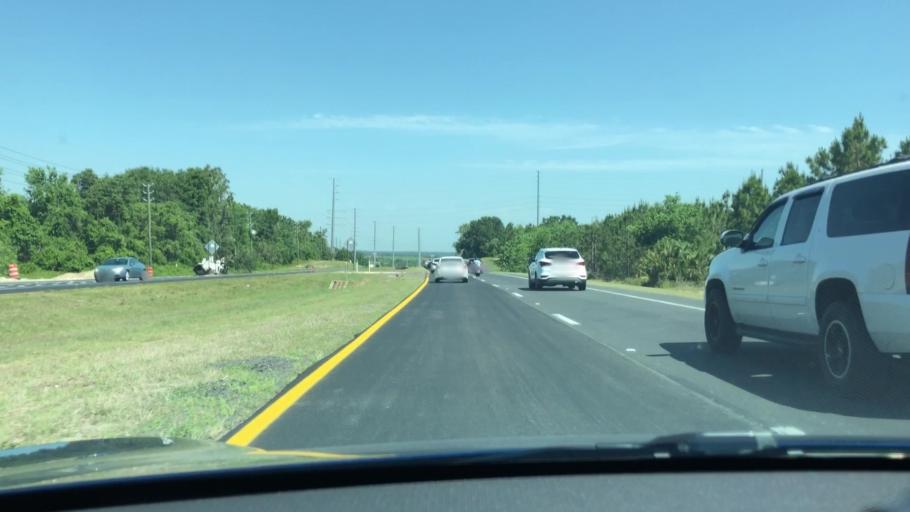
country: US
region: Florida
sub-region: Lake County
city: Minneola
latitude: 28.6056
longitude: -81.7562
